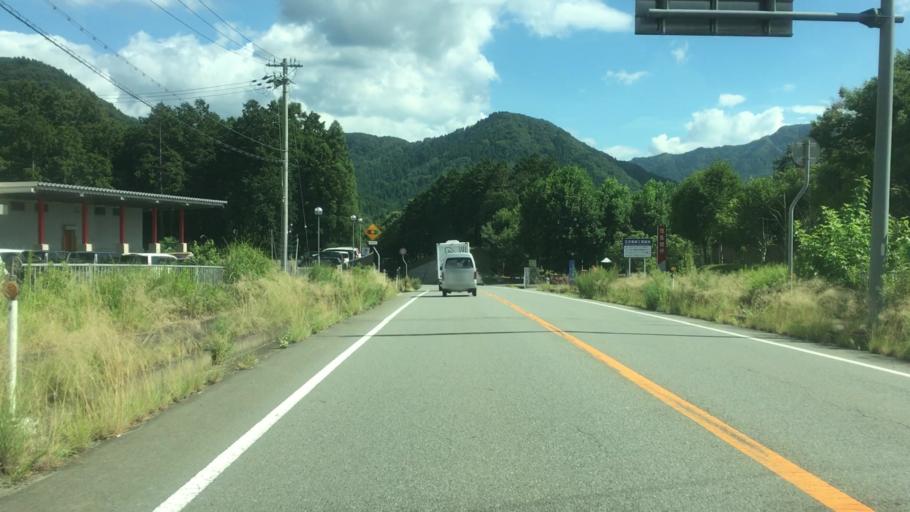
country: JP
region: Hyogo
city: Toyooka
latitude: 35.4631
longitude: 134.7328
